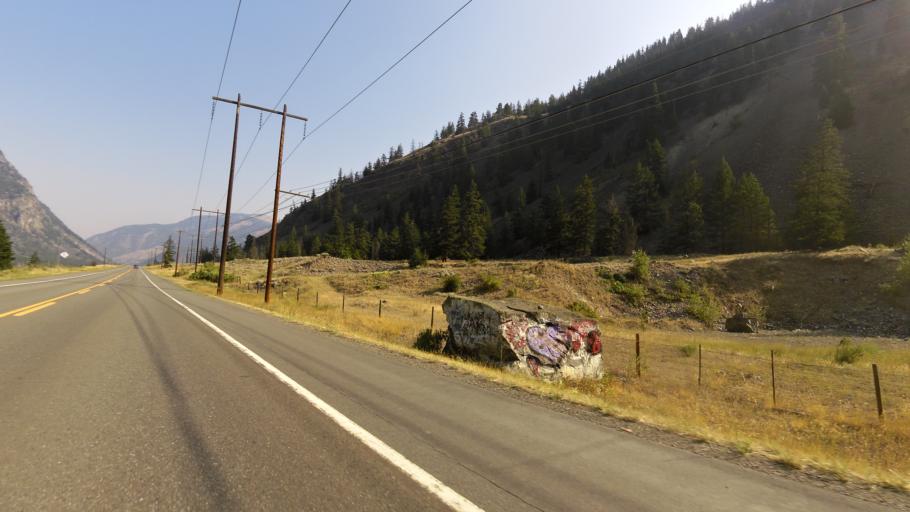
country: CA
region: British Columbia
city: Summerland
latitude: 49.2809
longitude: -120.0268
